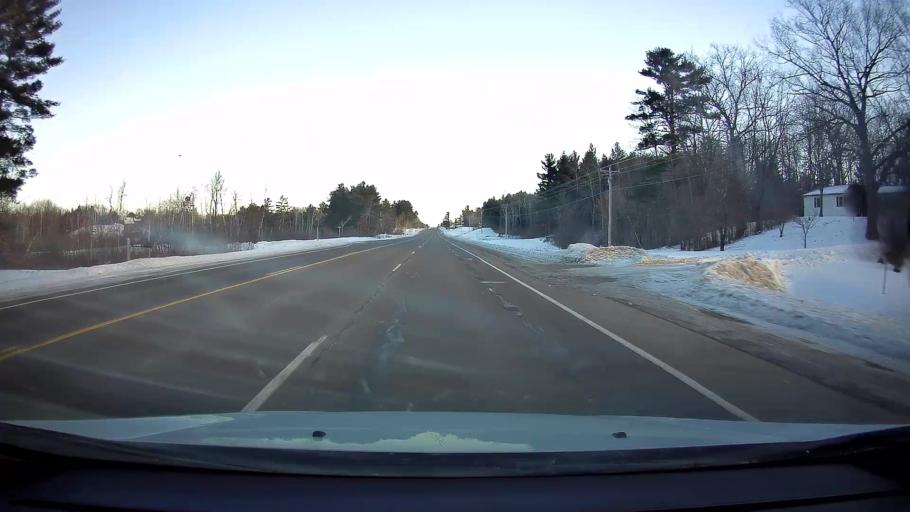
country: US
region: Wisconsin
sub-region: Barron County
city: Cumberland
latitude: 45.5664
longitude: -92.0173
